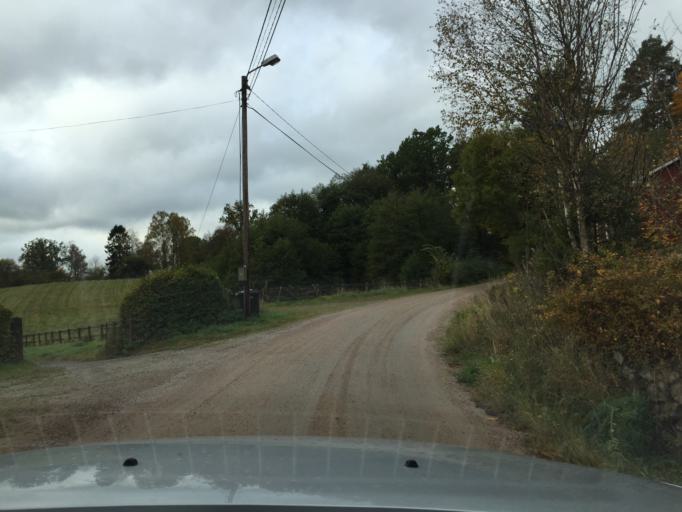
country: SE
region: Skane
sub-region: Hassleholms Kommun
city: Tormestorp
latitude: 56.0684
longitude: 13.7314
